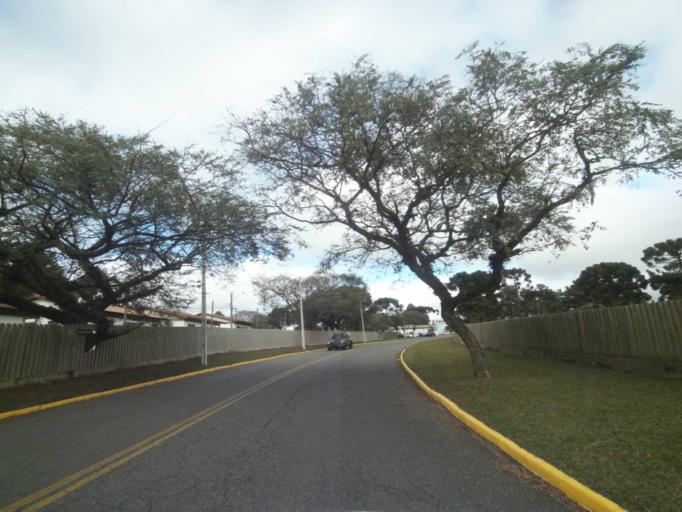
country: BR
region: Parana
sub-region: Sao Jose Dos Pinhais
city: Sao Jose dos Pinhais
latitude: -25.5266
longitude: -49.3022
